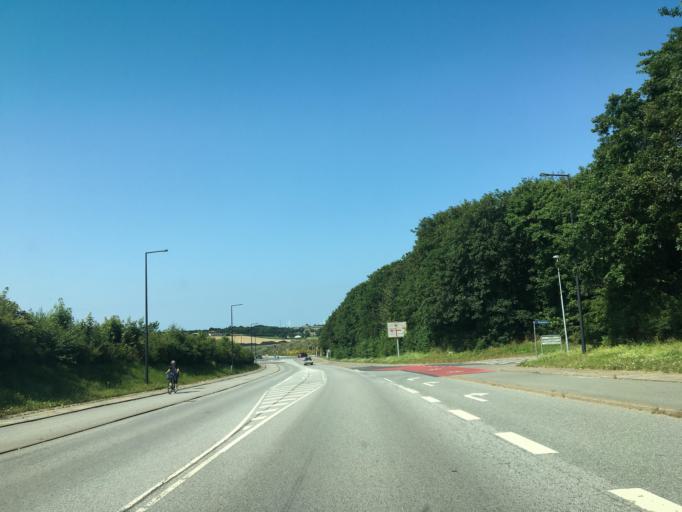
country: DK
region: North Denmark
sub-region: Thisted Kommune
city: Thisted
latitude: 56.9653
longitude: 8.6935
